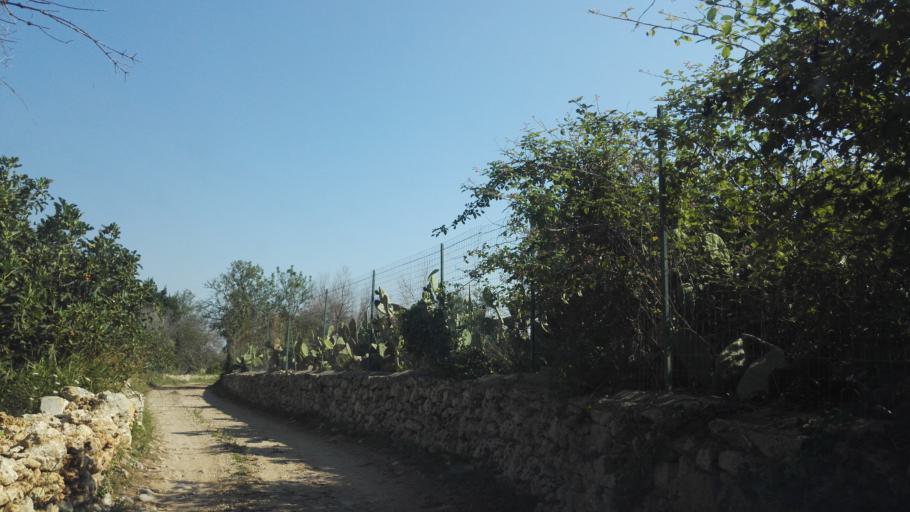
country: IT
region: Apulia
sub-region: Provincia di Lecce
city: Alezio
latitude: 40.0517
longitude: 18.0395
